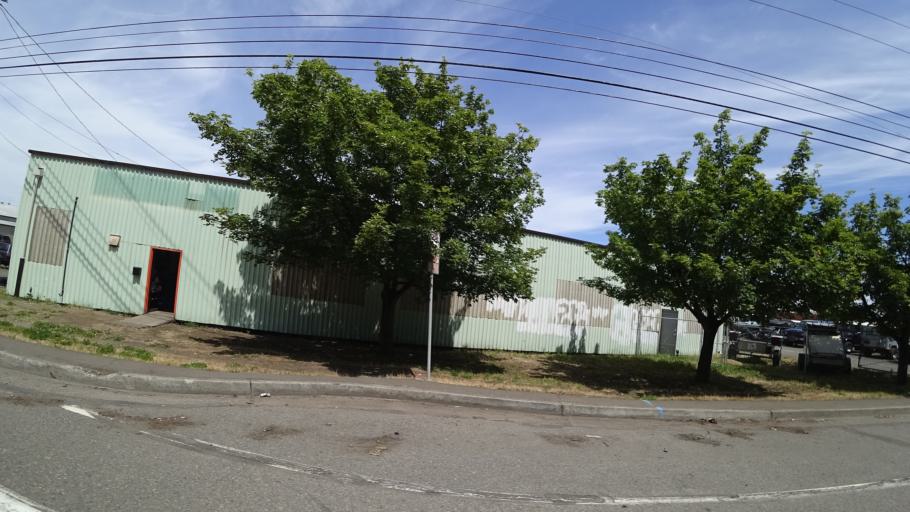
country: US
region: Oregon
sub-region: Multnomah County
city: Portland
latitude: 45.5453
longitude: -122.7229
